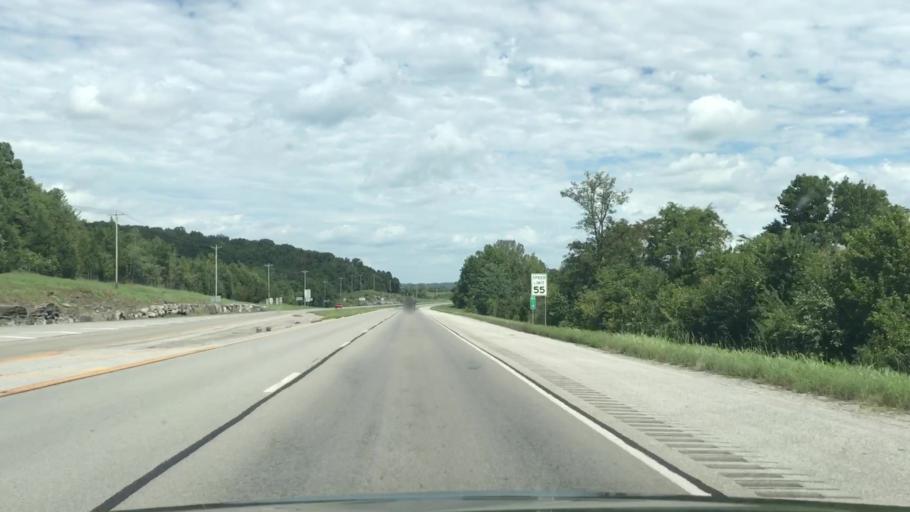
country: US
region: Kentucky
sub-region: Logan County
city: Russellville
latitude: 36.8437
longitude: -86.8637
